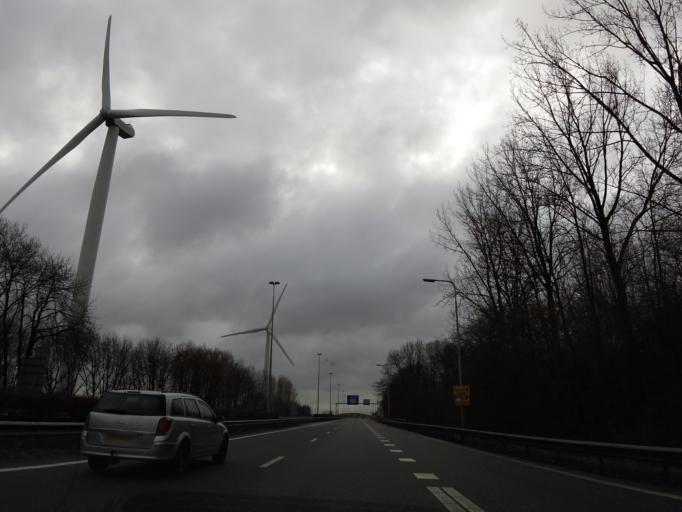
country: NL
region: Limburg
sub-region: Gemeente Simpelveld
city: Simpelveld
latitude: 50.8479
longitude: 6.0097
